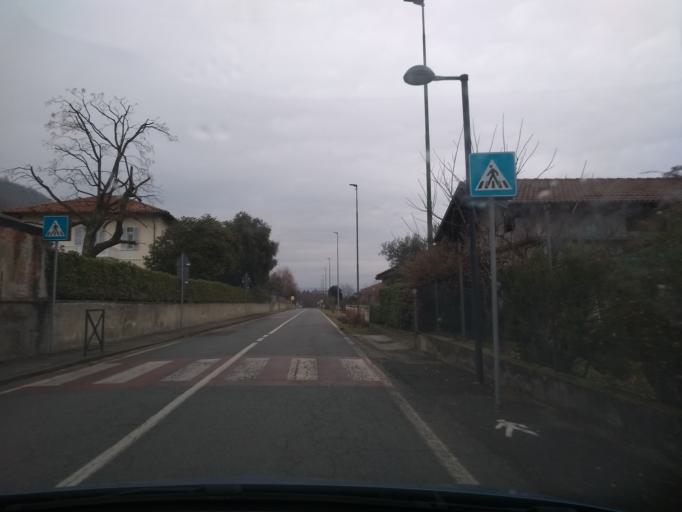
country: IT
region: Piedmont
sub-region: Provincia di Torino
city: Quagliuzzo
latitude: 45.4273
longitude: 7.7834
